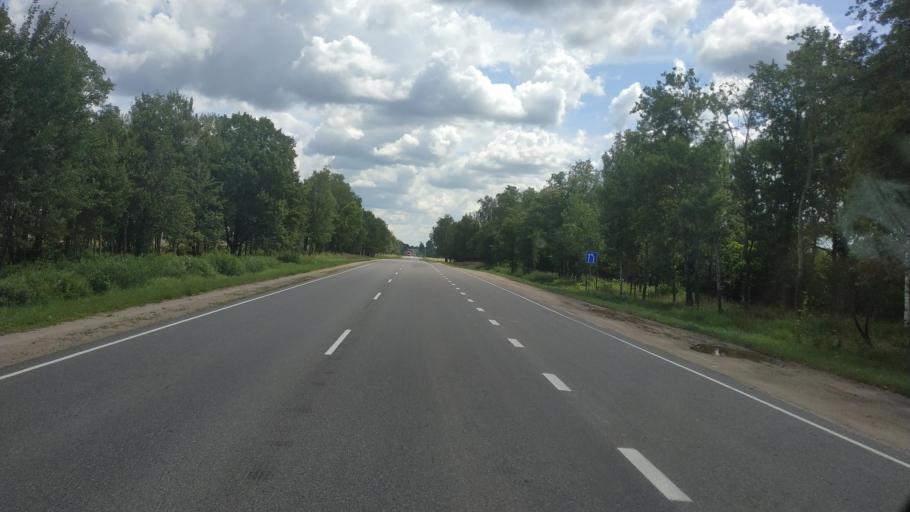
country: BY
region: Mogilev
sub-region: Mahilyowski Rayon
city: Veyno
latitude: 53.8197
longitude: 30.4372
